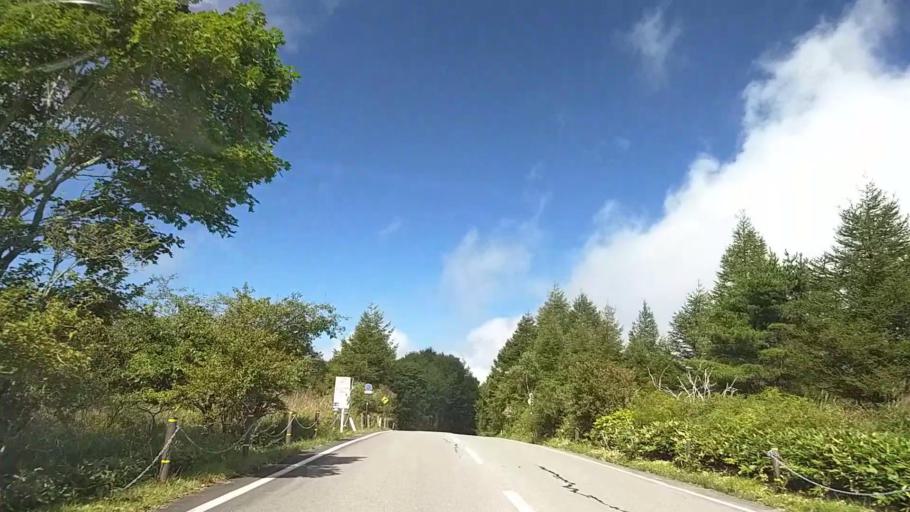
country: JP
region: Nagano
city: Suwa
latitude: 36.1170
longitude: 138.1600
